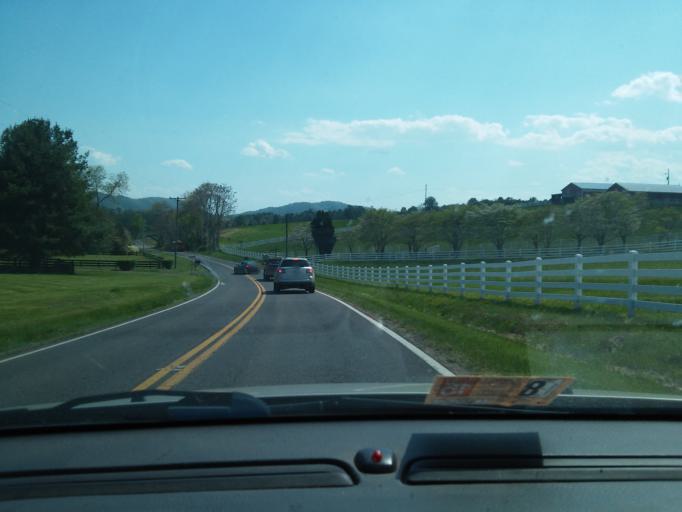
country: US
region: Virginia
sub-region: Madison County
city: Brightwood
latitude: 38.5595
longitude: -78.2356
